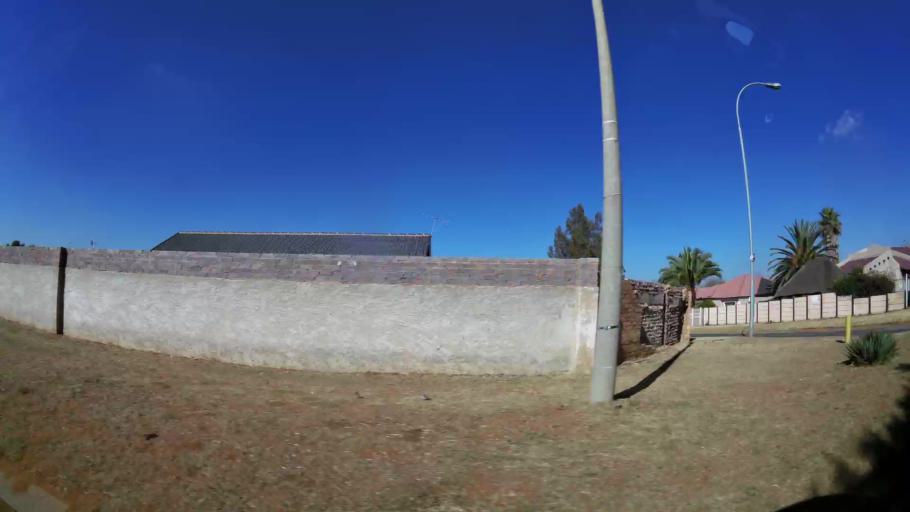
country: ZA
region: Gauteng
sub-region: City of Johannesburg Metropolitan Municipality
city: Roodepoort
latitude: -26.1655
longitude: 27.8278
